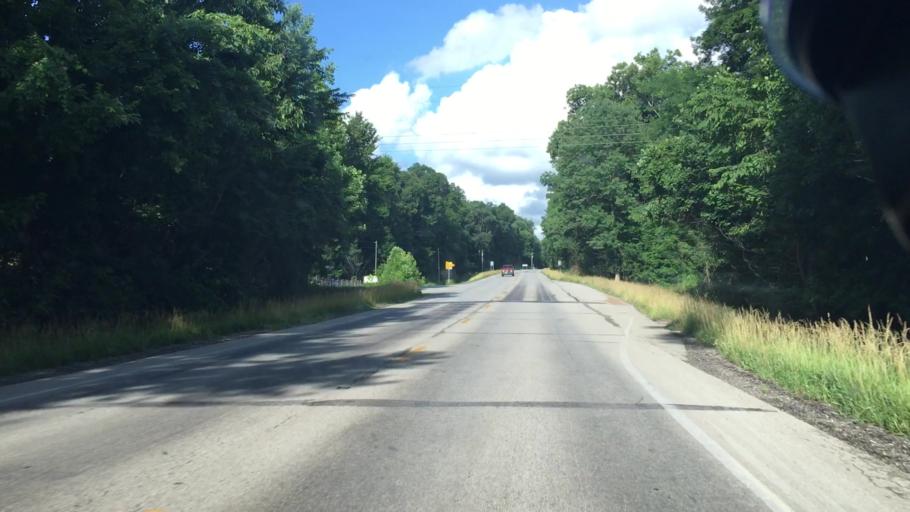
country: US
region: Indiana
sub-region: Perry County
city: Tell City
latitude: 38.0015
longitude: -86.8344
